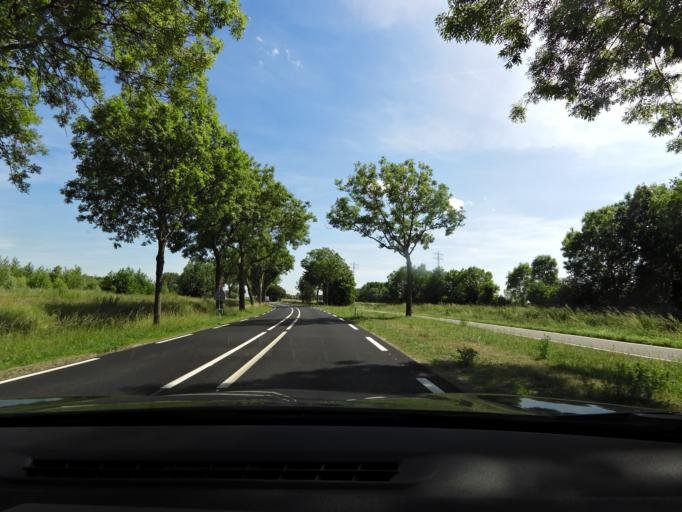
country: NL
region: South Holland
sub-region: Gemeente Maassluis
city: Maassluis
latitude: 51.8709
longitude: 4.2214
